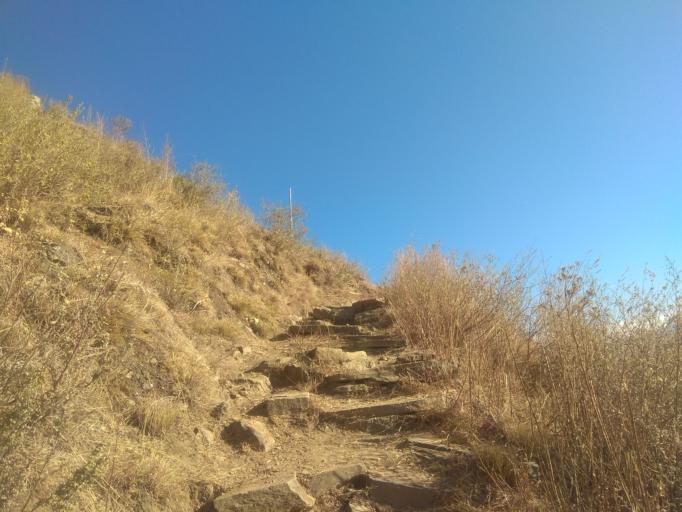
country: NP
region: Mid Western
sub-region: Bheri Zone
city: Dailekh
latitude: 29.2876
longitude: 81.7116
